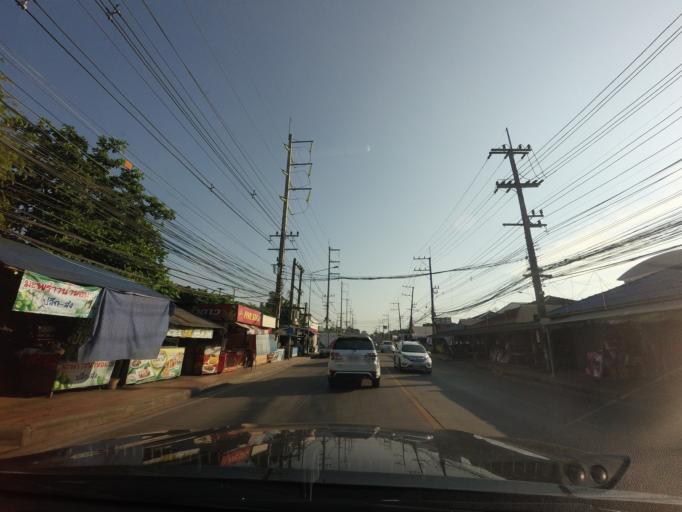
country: TH
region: Nan
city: Nan
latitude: 18.7731
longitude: 100.7655
